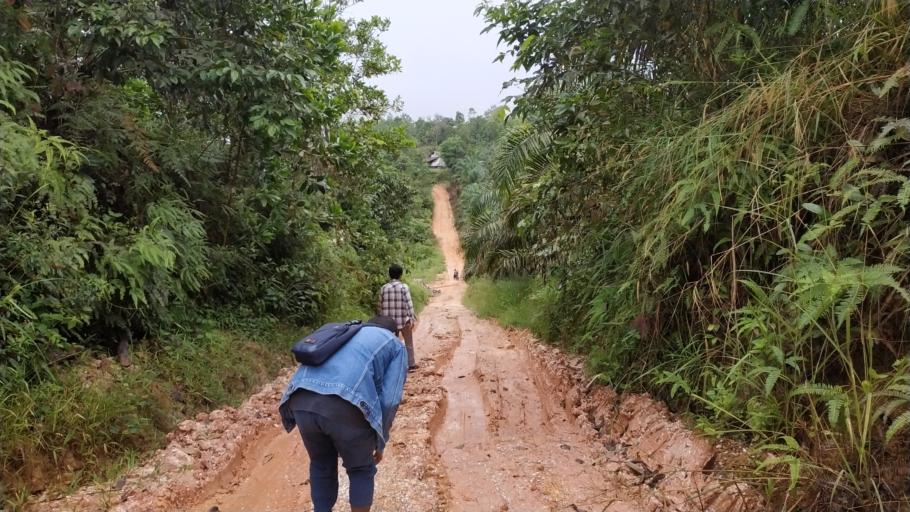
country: ID
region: Riau
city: Pekanbaru
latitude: 0.4848
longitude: 101.5645
